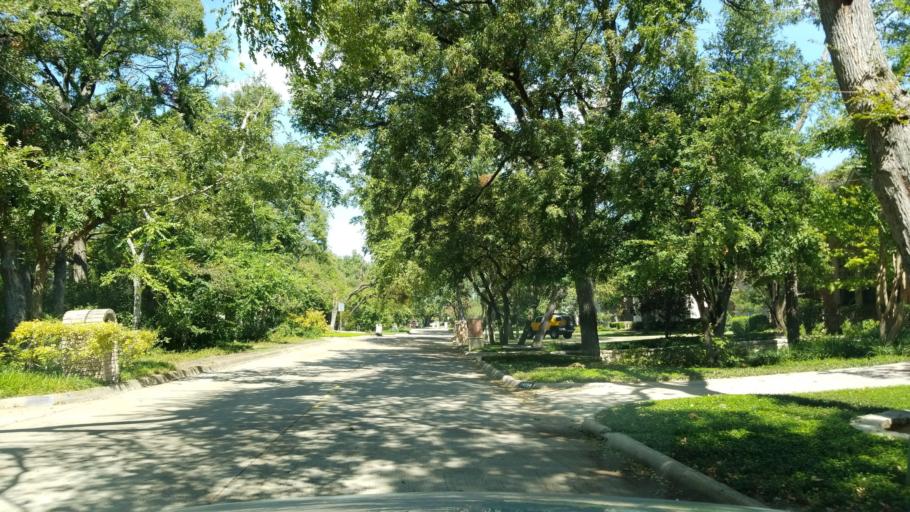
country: US
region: Texas
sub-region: Dallas County
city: Addison
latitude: 32.9494
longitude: -96.8105
